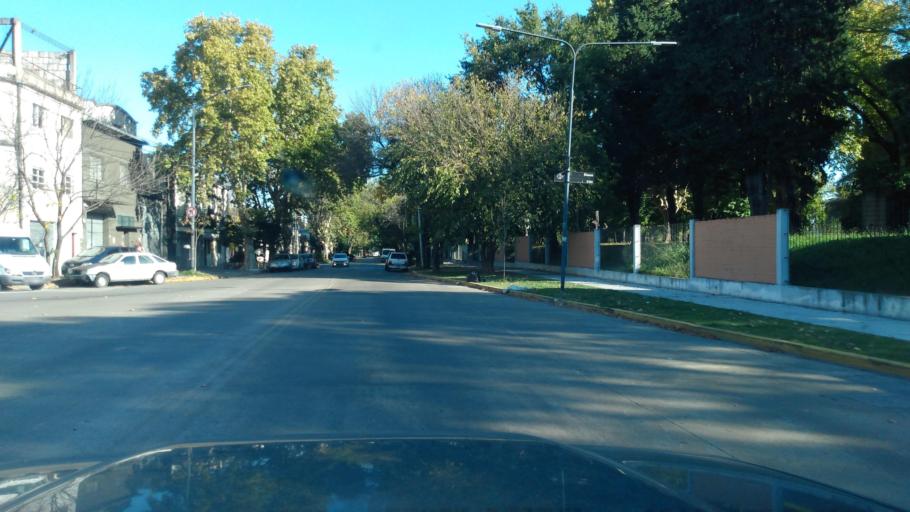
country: AR
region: Buenos Aires F.D.
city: Villa Santa Rita
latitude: -34.5934
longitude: -58.4701
